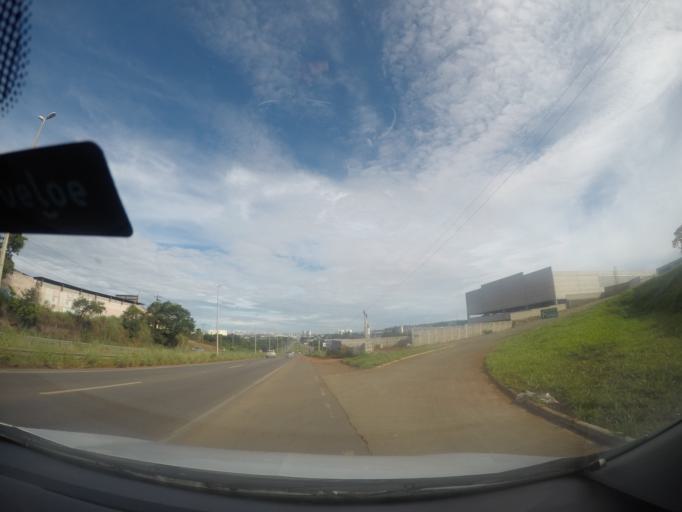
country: BR
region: Goias
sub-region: Goiania
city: Goiania
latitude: -16.6311
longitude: -49.3491
